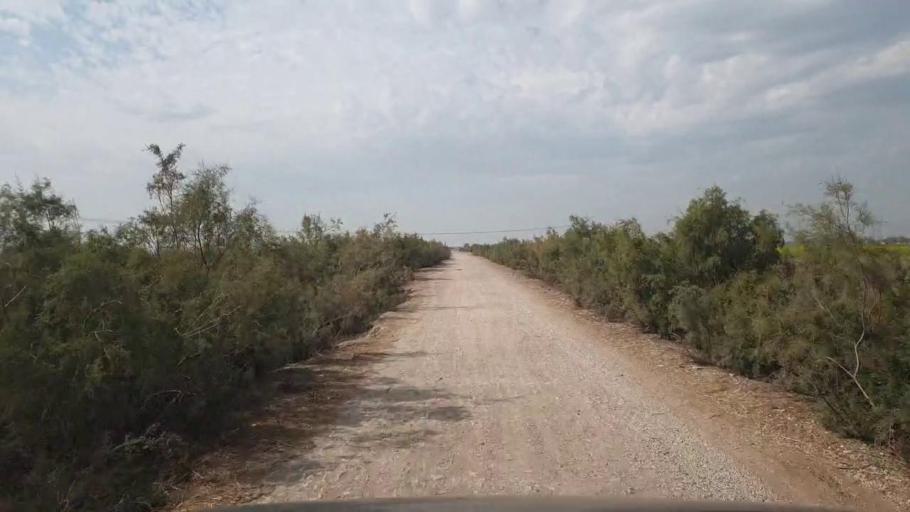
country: PK
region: Sindh
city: Sakrand
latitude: 26.0140
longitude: 68.3894
